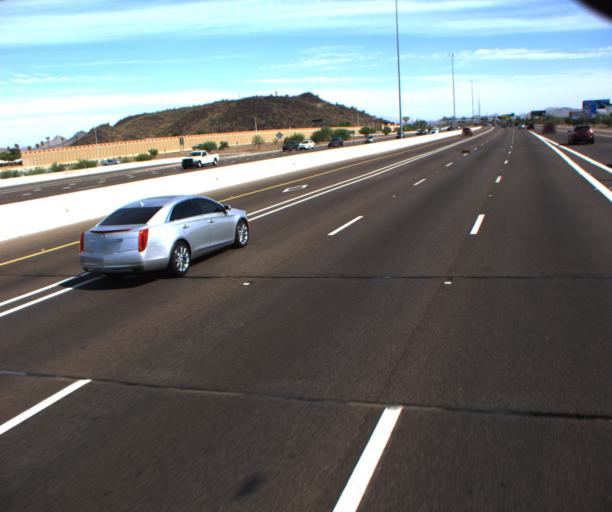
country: US
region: Arizona
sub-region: Maricopa County
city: Peoria
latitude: 33.6835
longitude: -112.1122
